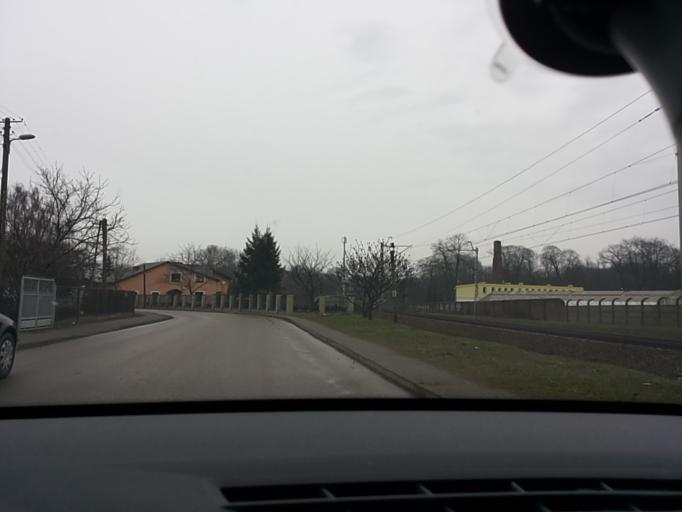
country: PL
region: Lodz Voivodeship
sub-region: Skierniewice
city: Skierniewice
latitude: 51.9615
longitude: 20.1348
